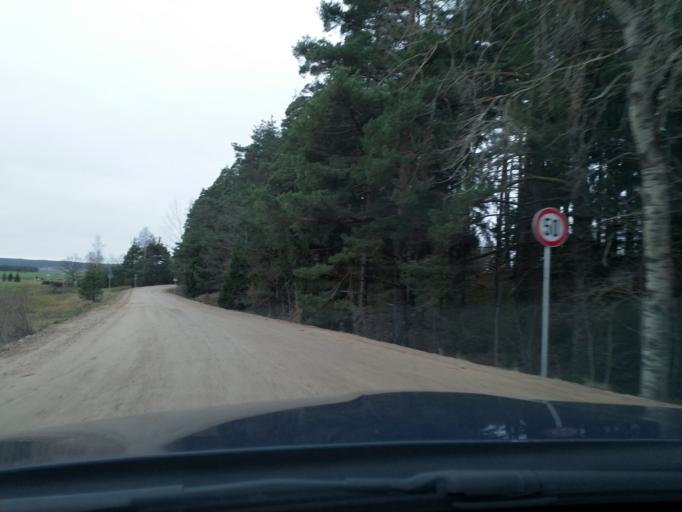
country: LV
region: Ventspils Rajons
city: Piltene
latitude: 57.1278
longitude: 21.8060
